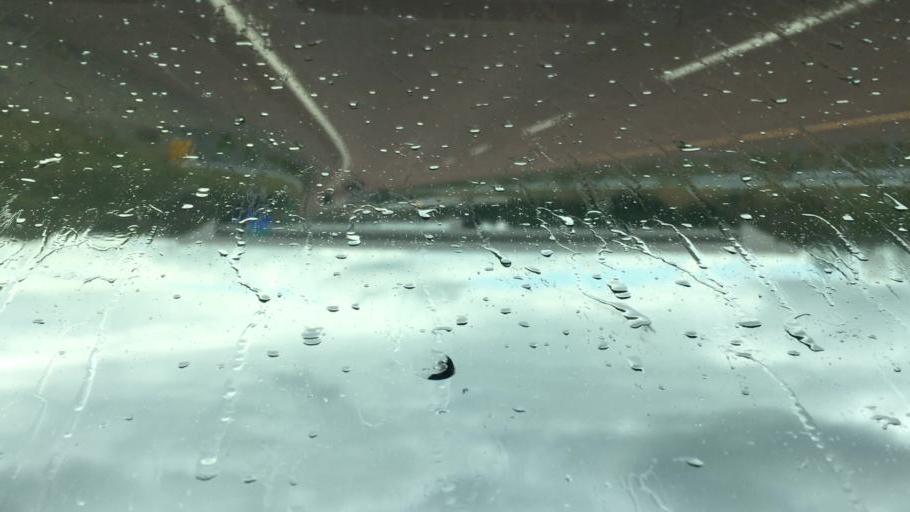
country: CA
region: Nova Scotia
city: Antigonish
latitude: 45.6038
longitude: -61.9207
